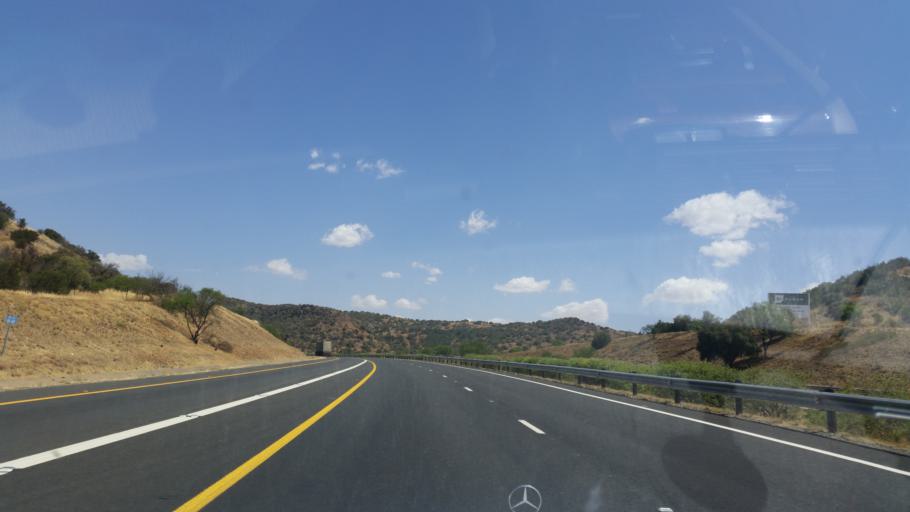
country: ZA
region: Orange Free State
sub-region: Mangaung Metropolitan Municipality
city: Bloemfontein
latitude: -28.9791
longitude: 26.2845
